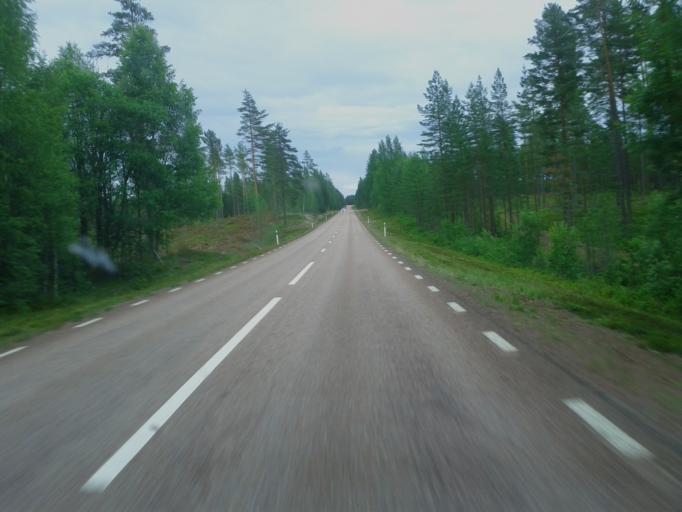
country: SE
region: Dalarna
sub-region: Mora Kommun
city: Mora
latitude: 61.0735
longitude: 14.3592
